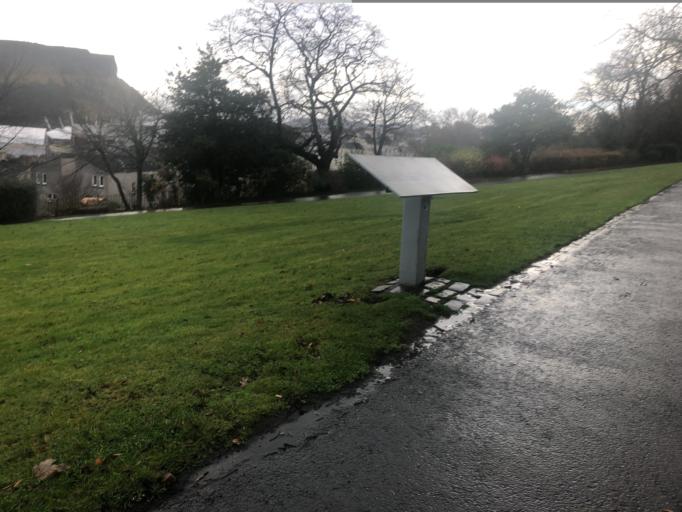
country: GB
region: Scotland
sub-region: Edinburgh
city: Edinburgh
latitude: 55.9549
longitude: -3.1748
